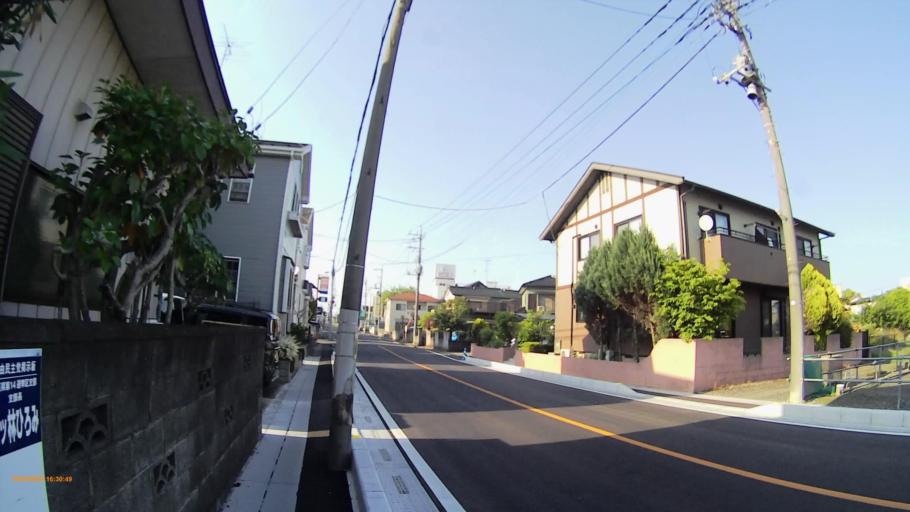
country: JP
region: Saitama
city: Satte
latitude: 36.0822
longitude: 139.7217
